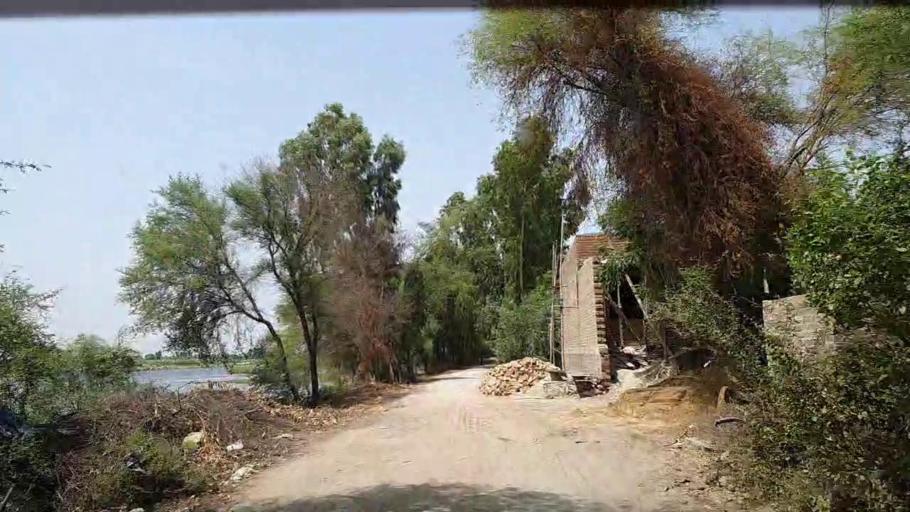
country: PK
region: Sindh
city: Ghotki
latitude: 28.0865
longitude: 69.3110
